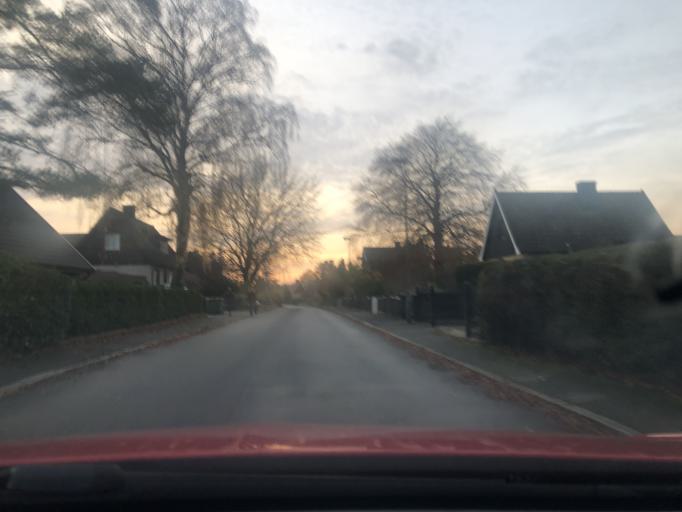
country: SE
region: Skane
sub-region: Burlovs Kommun
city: Arloev
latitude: 55.5964
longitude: 13.0845
